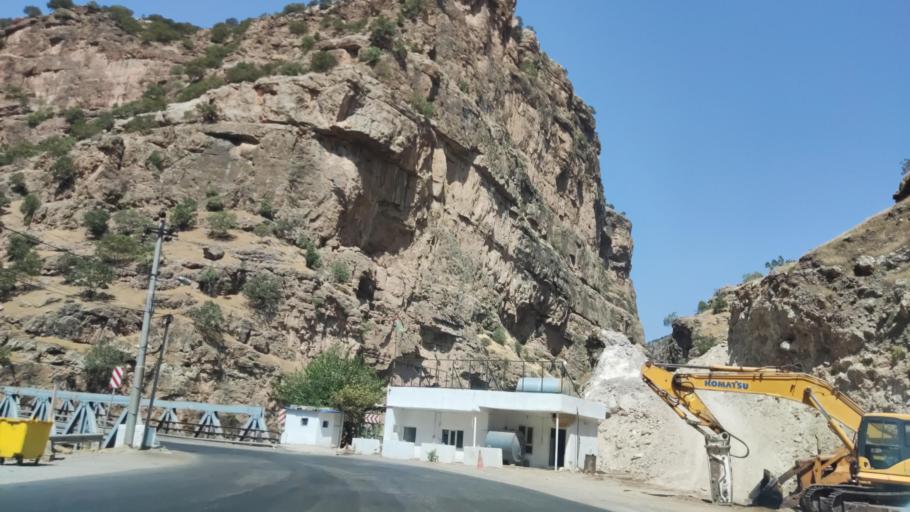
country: IQ
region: Arbil
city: Ruwandiz
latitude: 36.6297
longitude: 44.4574
